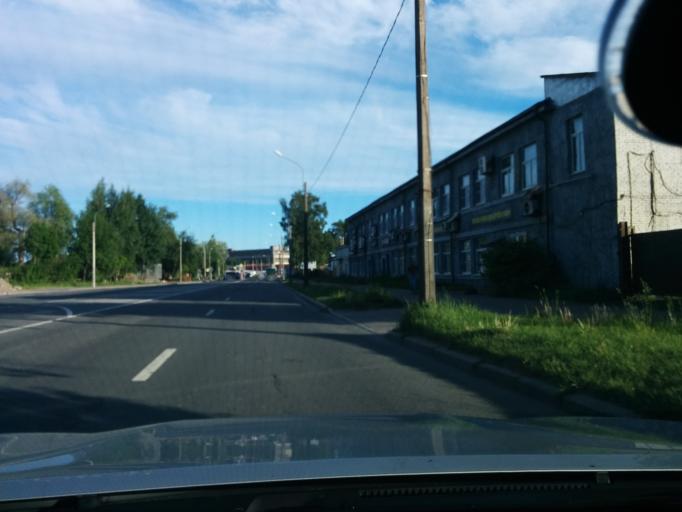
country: RU
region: Leningrad
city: Finlyandskiy
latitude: 59.9795
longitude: 30.3664
